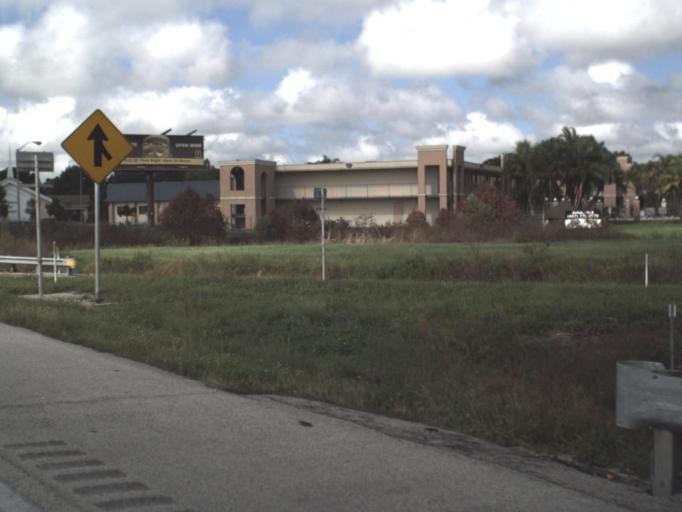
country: US
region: Florida
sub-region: Polk County
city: Gibsonia
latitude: 28.1027
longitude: -81.9479
